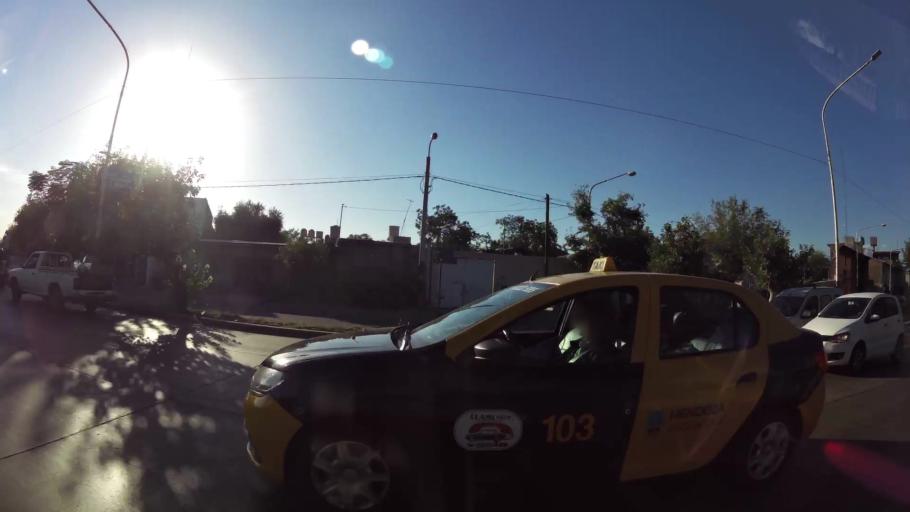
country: AR
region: Mendoza
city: Mendoza
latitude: -32.8768
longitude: -68.8261
